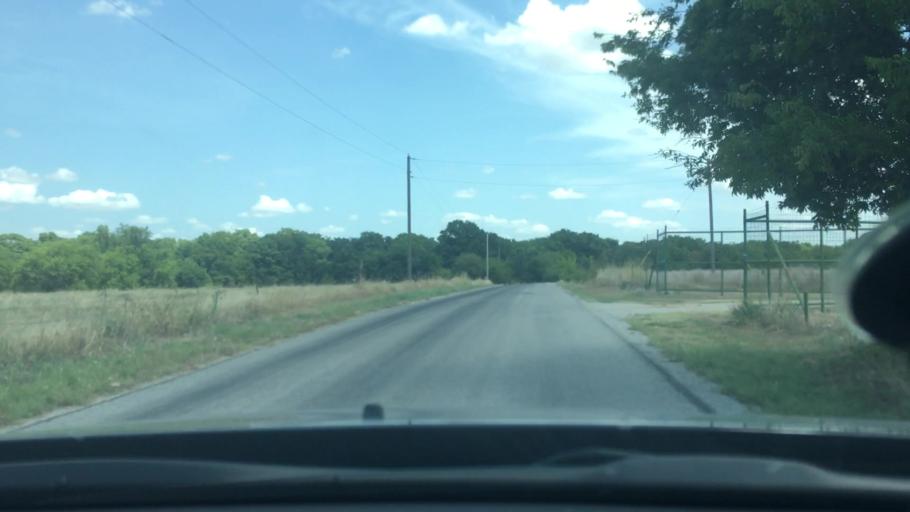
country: US
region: Oklahoma
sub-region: Love County
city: Marietta
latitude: 34.0003
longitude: -97.1870
